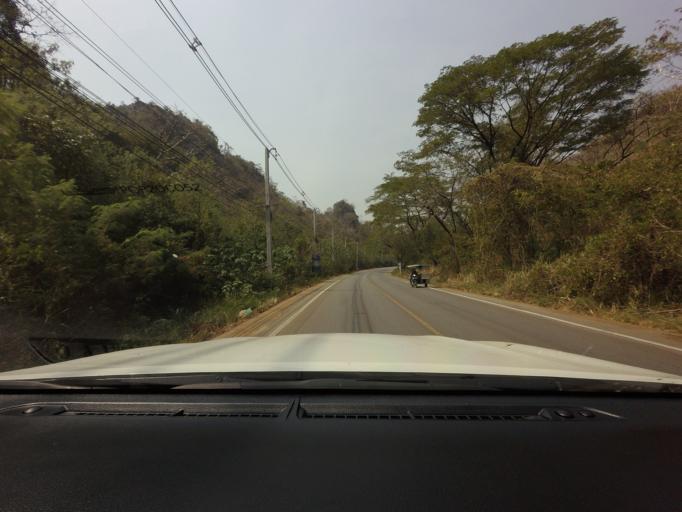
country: TH
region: Sara Buri
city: Muak Lek
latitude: 14.5739
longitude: 101.2793
